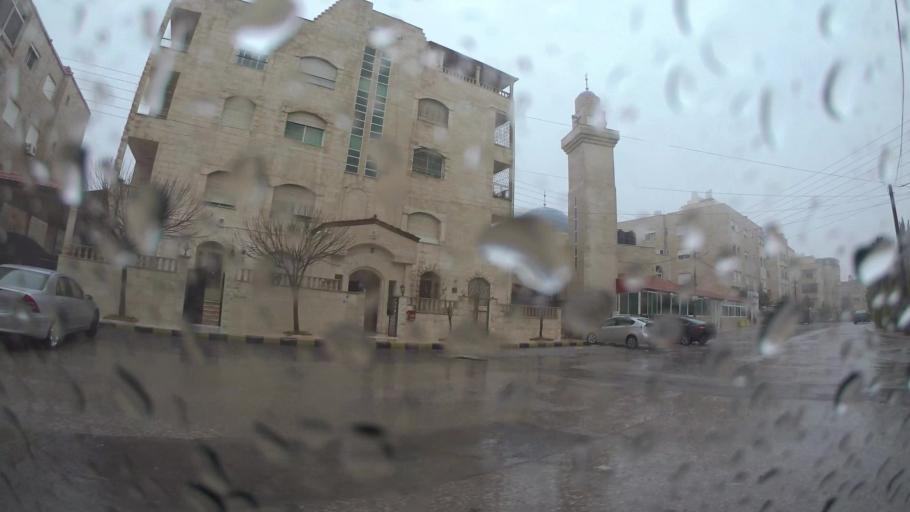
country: JO
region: Amman
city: Al Jubayhah
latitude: 32.0177
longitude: 35.8843
